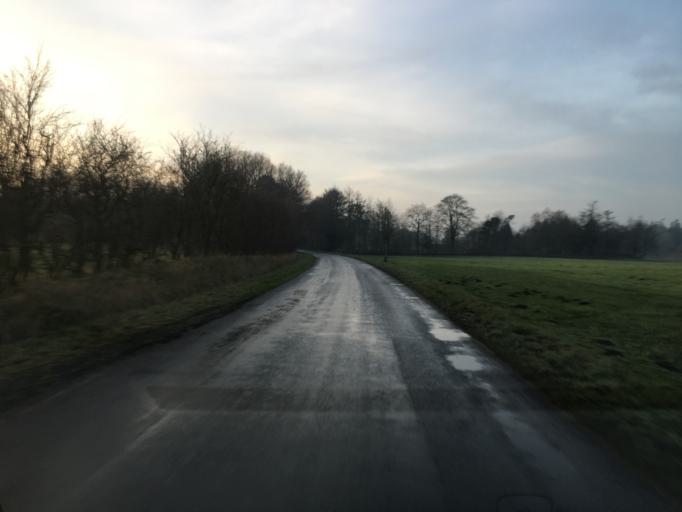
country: DK
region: South Denmark
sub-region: Tonder Kommune
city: Logumkloster
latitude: 55.1156
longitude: 8.9669
